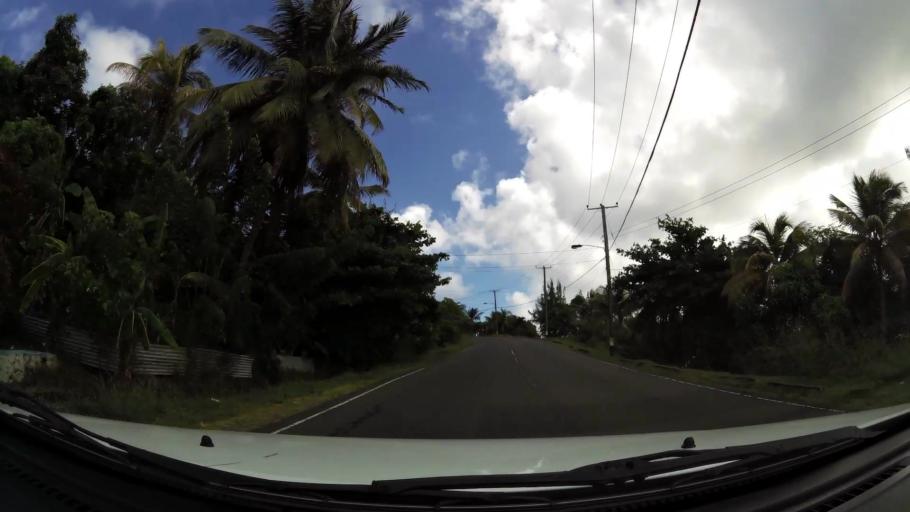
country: LC
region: Dennery Quarter
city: Dennery
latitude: 13.9158
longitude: -60.8941
